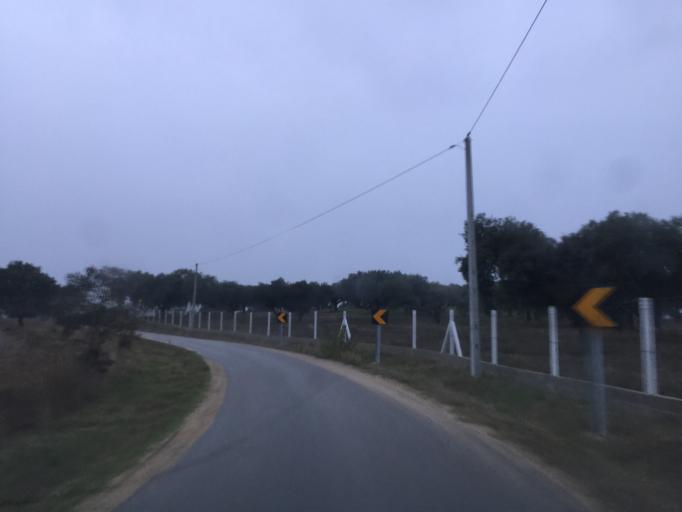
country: PT
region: Portalegre
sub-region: Avis
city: Avis
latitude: 39.0495
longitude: -7.9050
